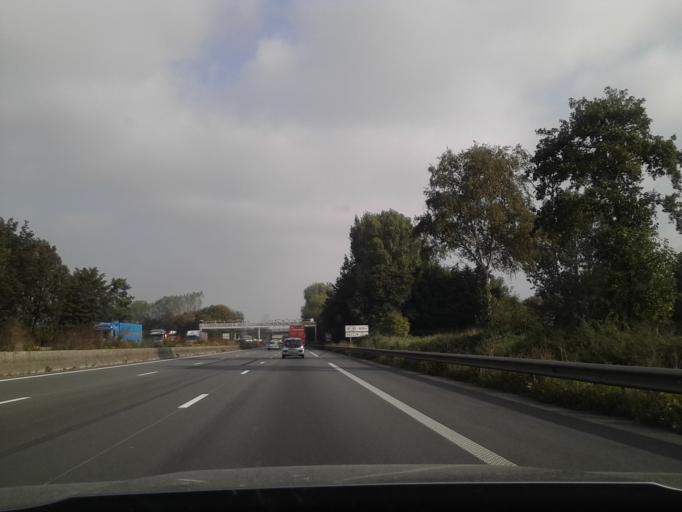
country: FR
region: Nord-Pas-de-Calais
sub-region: Departement du Nord
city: Attiches
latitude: 50.5353
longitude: 3.0495
